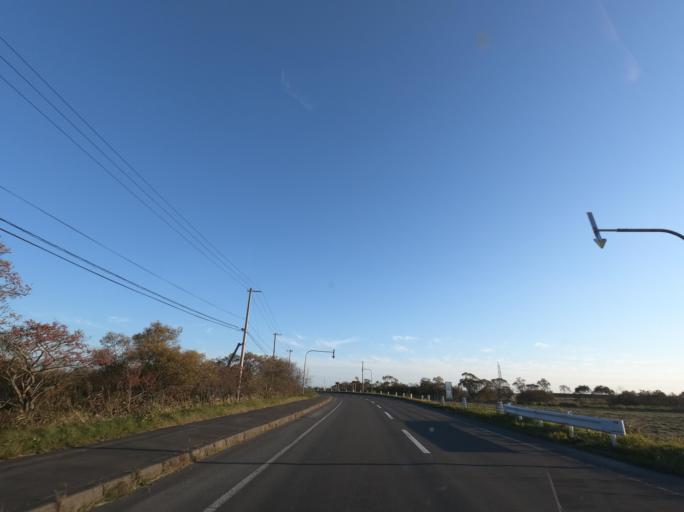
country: JP
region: Hokkaido
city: Kushiro
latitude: 43.0571
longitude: 144.2844
